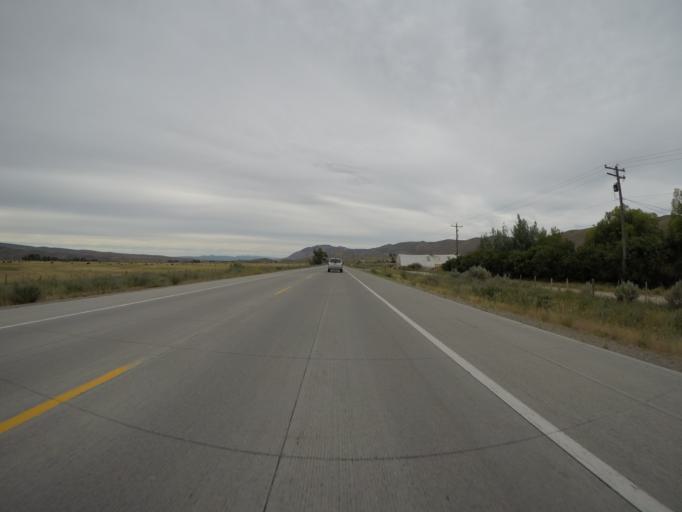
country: US
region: Idaho
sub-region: Bear Lake County
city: Montpelier
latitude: 42.0975
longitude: -110.9522
